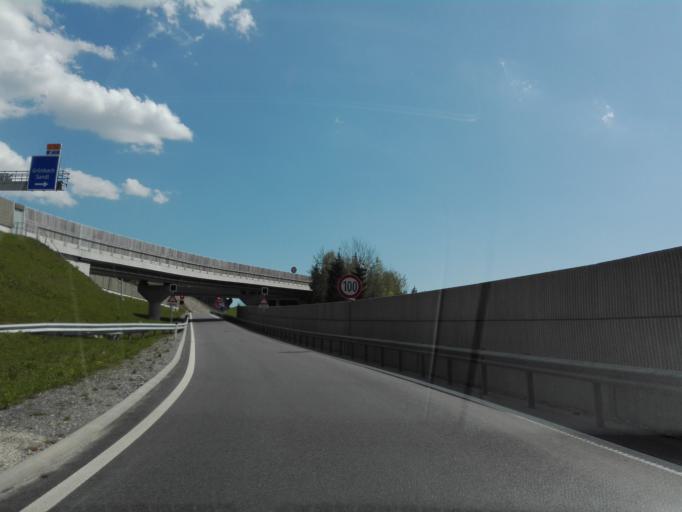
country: AT
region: Upper Austria
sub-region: Politischer Bezirk Freistadt
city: Freistadt
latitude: 48.5180
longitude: 14.5150
